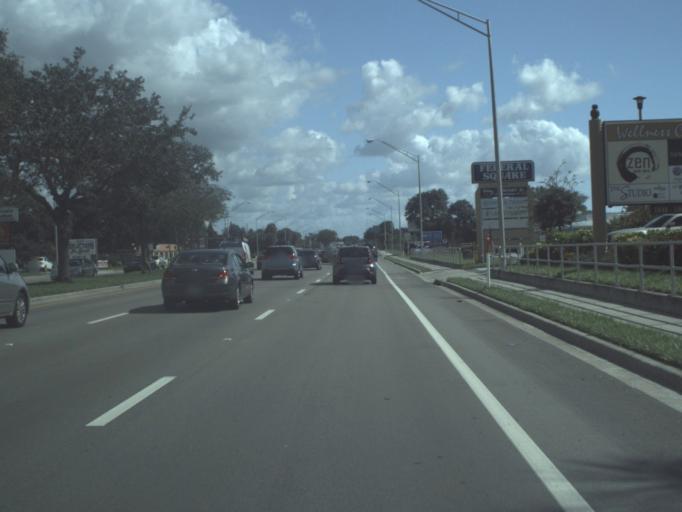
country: US
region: Florida
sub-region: Sarasota County
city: South Venice
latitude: 27.0602
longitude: -82.4152
